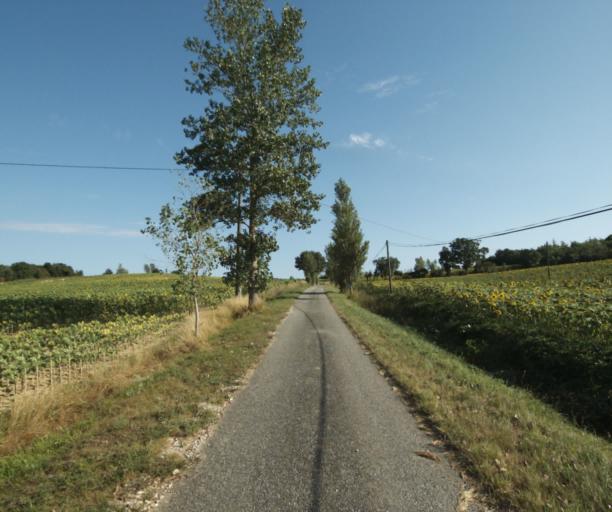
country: FR
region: Midi-Pyrenees
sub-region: Departement de la Haute-Garonne
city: Saint-Felix-Lauragais
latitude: 43.4431
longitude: 1.8124
